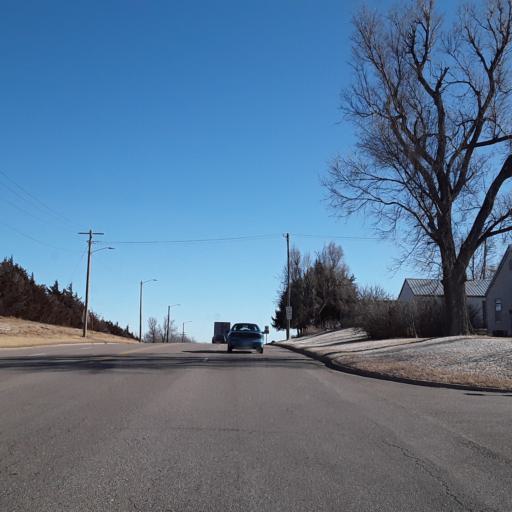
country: US
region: Kansas
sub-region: Pawnee County
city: Larned
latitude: 38.1881
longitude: -99.0946
